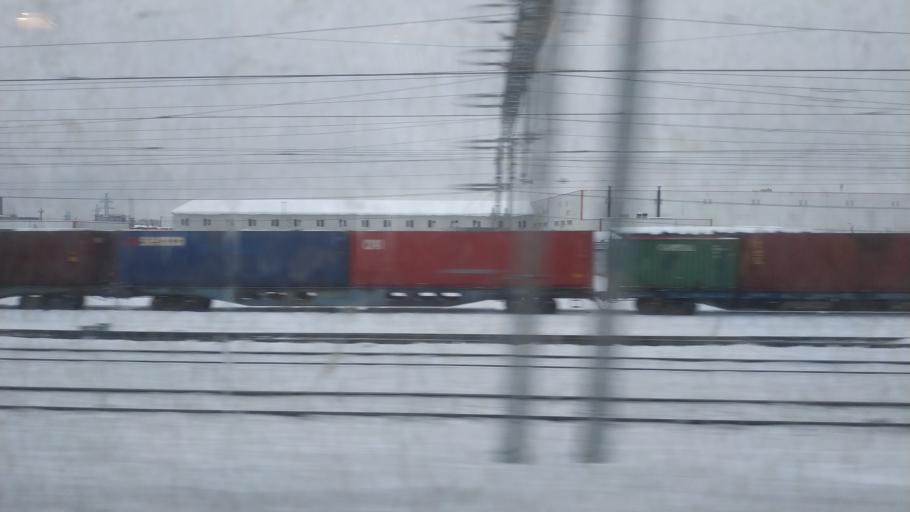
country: RU
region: Moskovskaya
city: Shcherbinka
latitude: 55.4844
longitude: 37.5548
